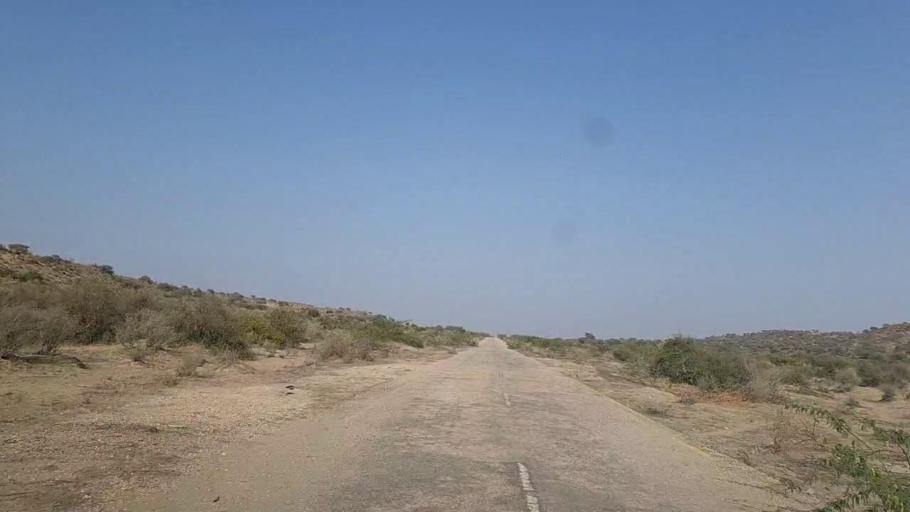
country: PK
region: Sindh
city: Naukot
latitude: 24.6000
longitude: 69.3230
